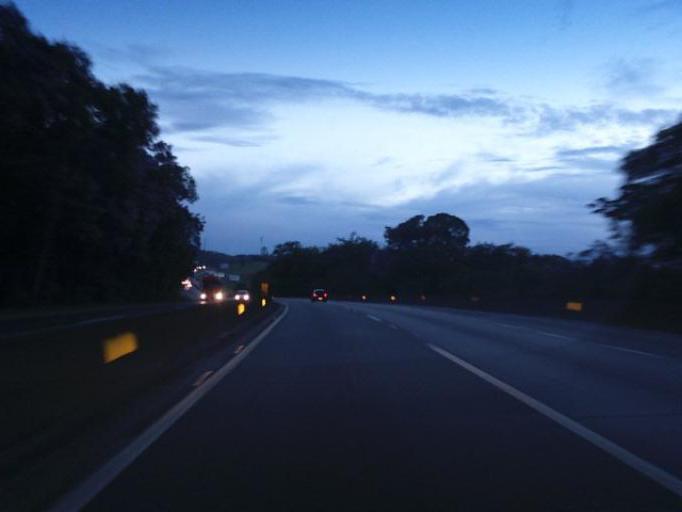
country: BR
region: Santa Catarina
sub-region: Joinville
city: Joinville
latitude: -26.4015
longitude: -48.8398
